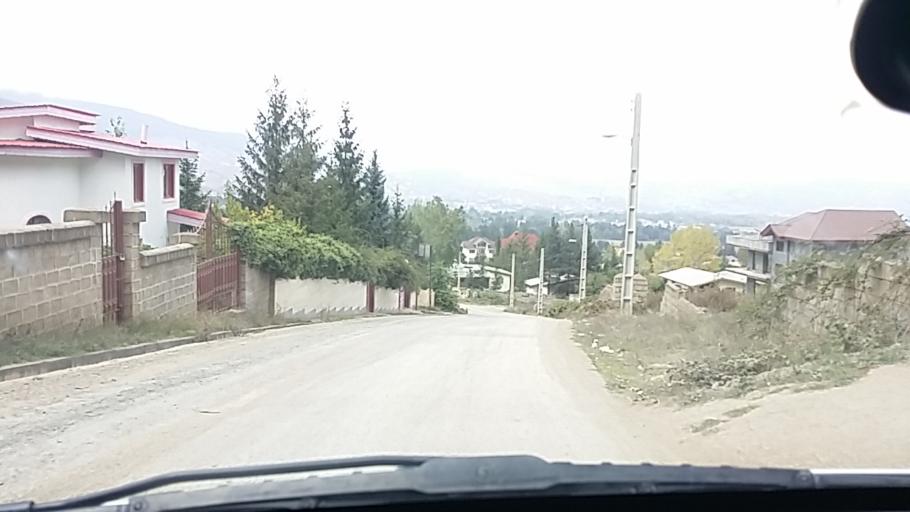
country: IR
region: Mazandaran
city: `Abbasabad
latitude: 36.4941
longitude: 51.1654
